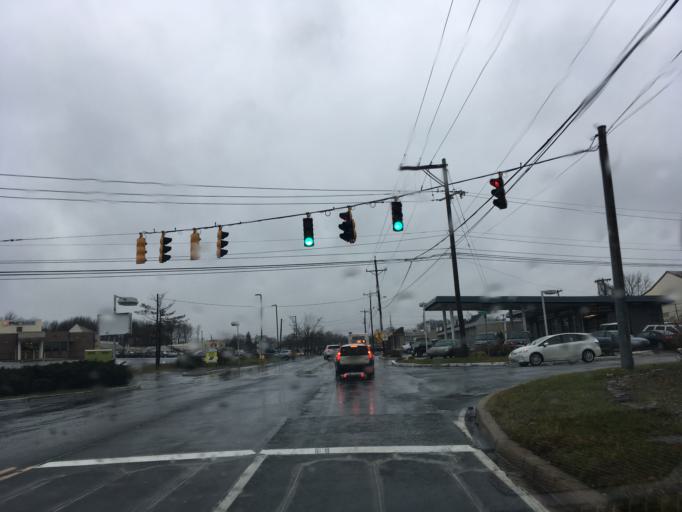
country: US
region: Delaware
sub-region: New Castle County
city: Bellefonte
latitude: 39.7998
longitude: -75.5052
